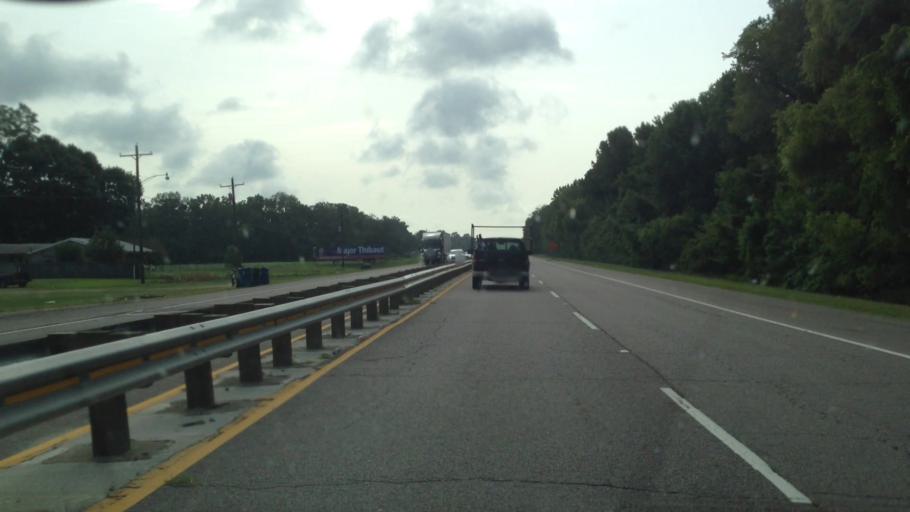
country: US
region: Louisiana
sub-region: Pointe Coupee Parish
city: Livonia
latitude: 30.5542
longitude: -91.5357
